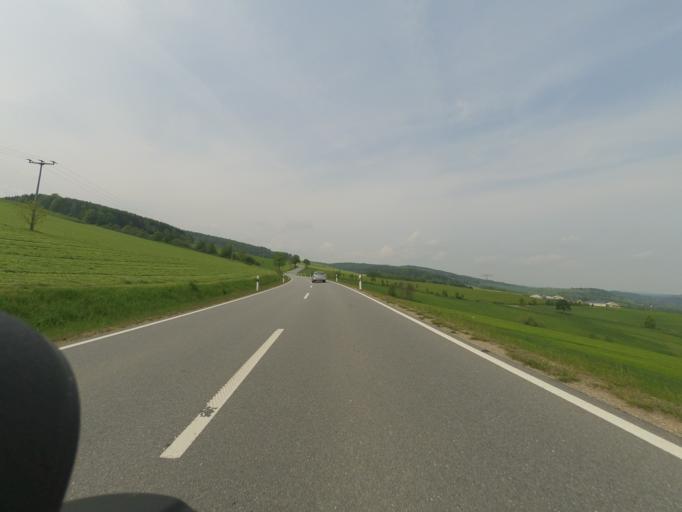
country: DE
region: Saxony
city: Olbernhau
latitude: 50.6563
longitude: 13.3144
